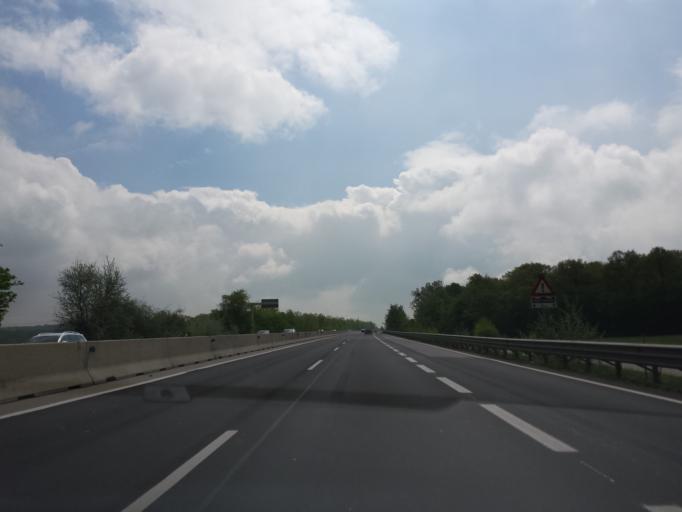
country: AT
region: Lower Austria
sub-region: Politischer Bezirk Wien-Umgebung
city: Fischamend Dorf
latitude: 48.0925
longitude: 16.6637
